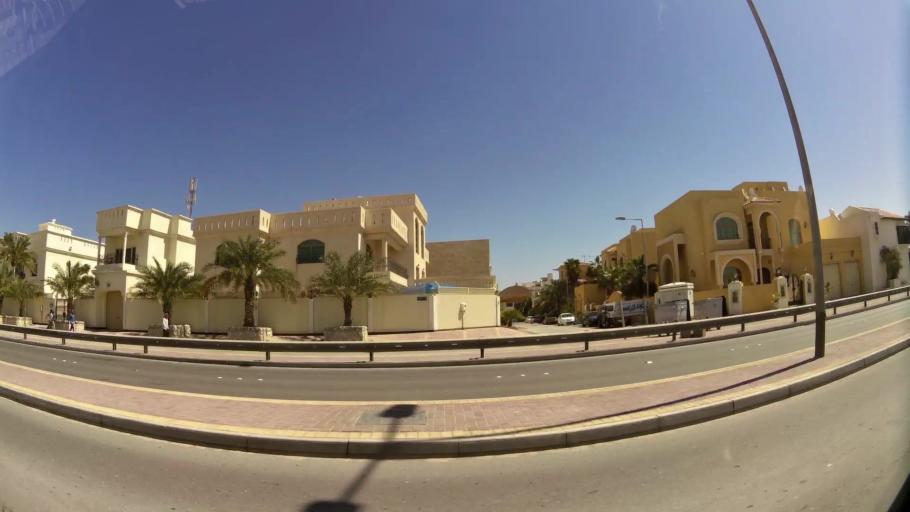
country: BH
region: Muharraq
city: Al Muharraq
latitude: 26.2677
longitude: 50.6030
